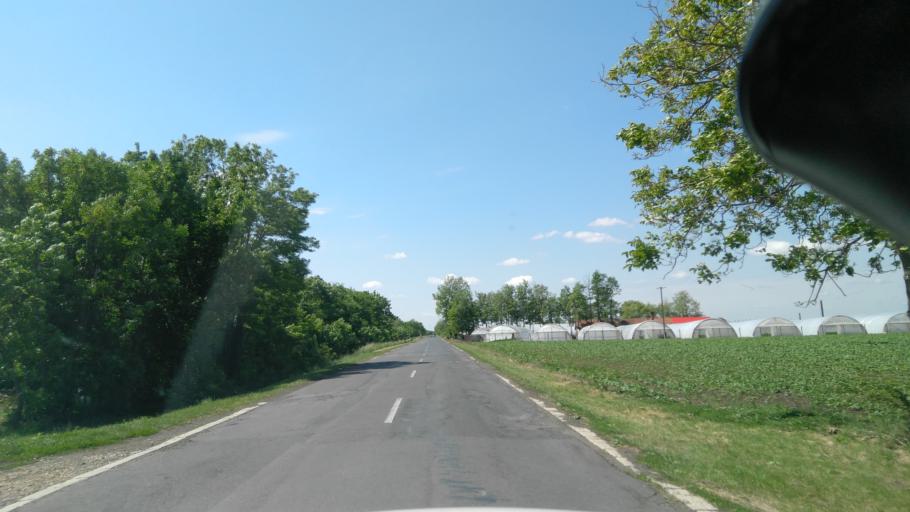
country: HU
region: Bekes
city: Medgyesegyhaza
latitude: 46.4853
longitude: 21.0241
